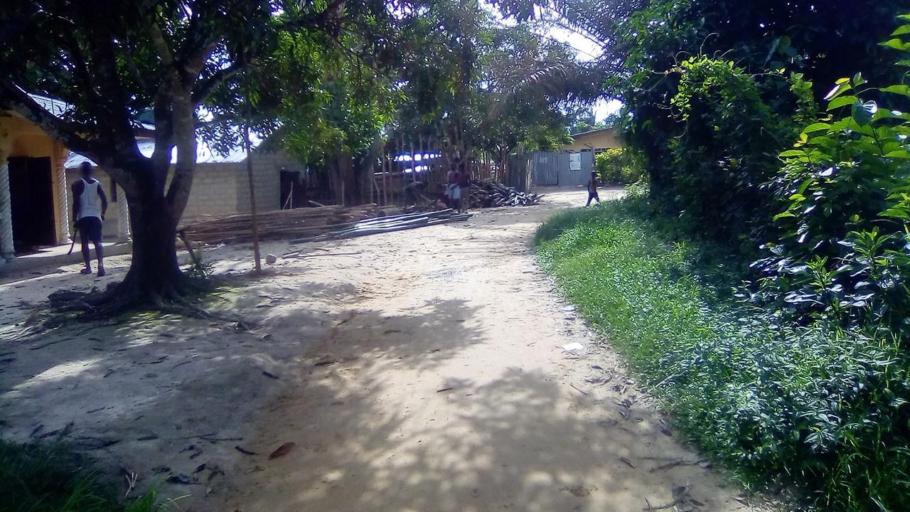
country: SL
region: Southern Province
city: Pujehun
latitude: 7.3639
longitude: -11.7233
